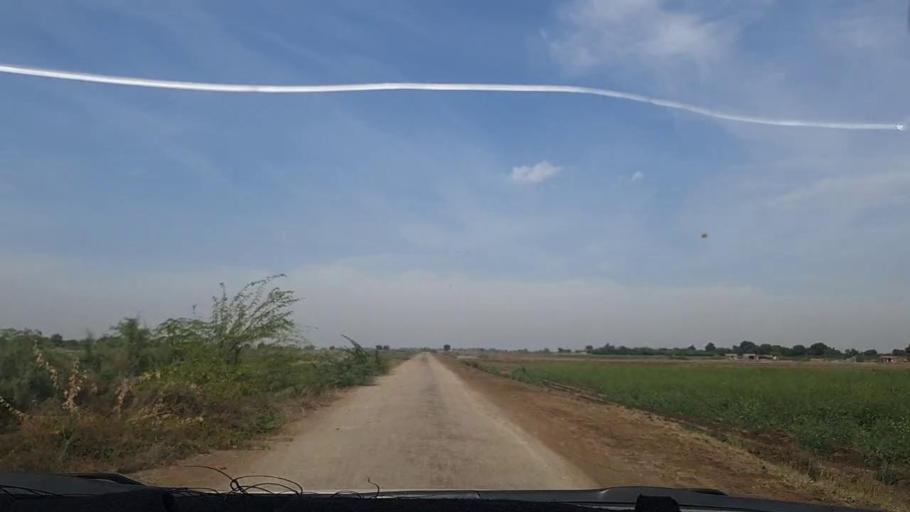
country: PK
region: Sindh
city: Pithoro
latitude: 25.4668
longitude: 69.4702
